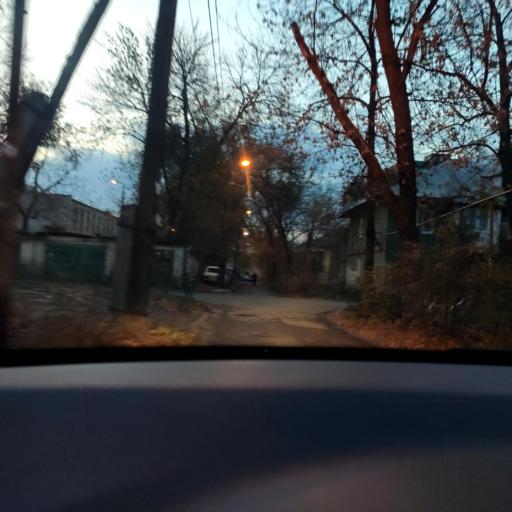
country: RU
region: Samara
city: Samara
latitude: 53.2224
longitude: 50.2458
